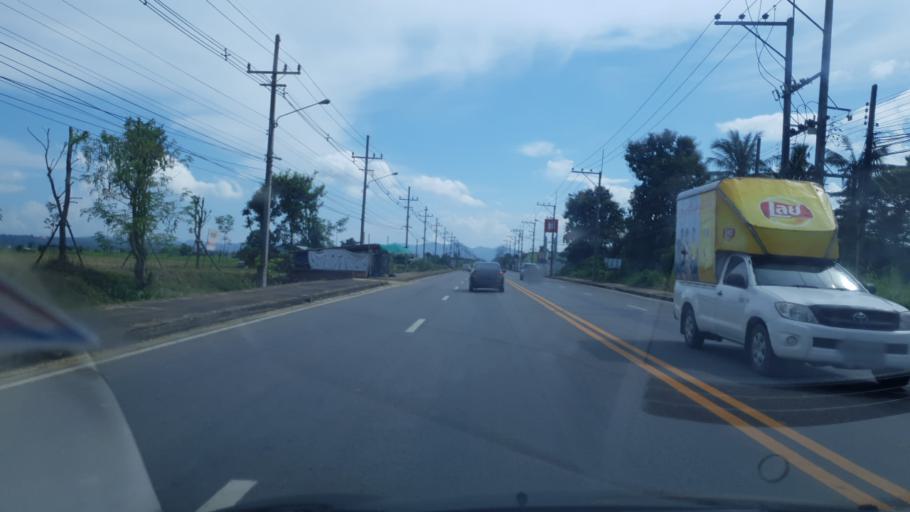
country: TH
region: Chiang Rai
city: Wiang Pa Pao
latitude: 19.2313
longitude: 99.5157
